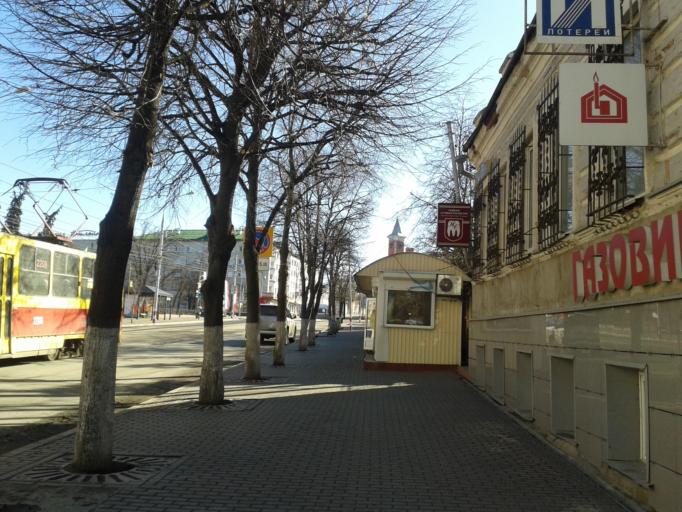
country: RU
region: Ulyanovsk
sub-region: Ulyanovskiy Rayon
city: Ulyanovsk
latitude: 54.3142
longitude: 48.3941
